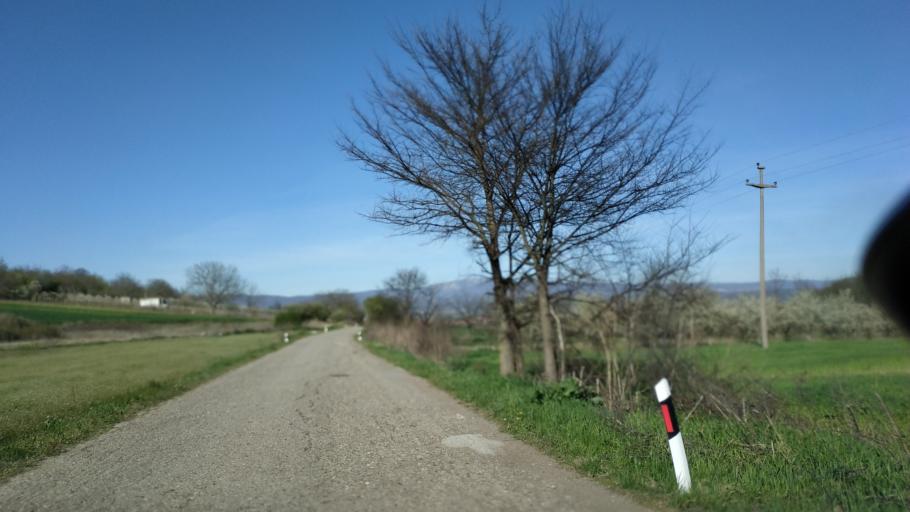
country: RS
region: Central Serbia
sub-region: Nisavski Okrug
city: Aleksinac
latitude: 43.4942
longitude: 21.6718
